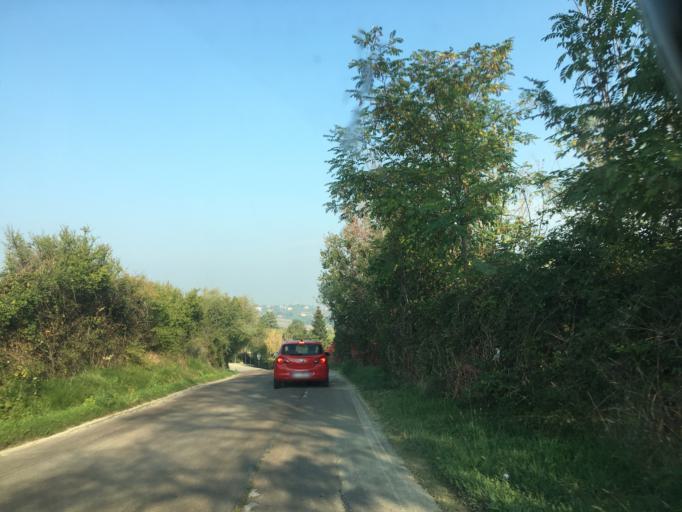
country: IT
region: Emilia-Romagna
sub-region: Provincia di Rimini
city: San Clemente
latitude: 43.9450
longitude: 12.6203
